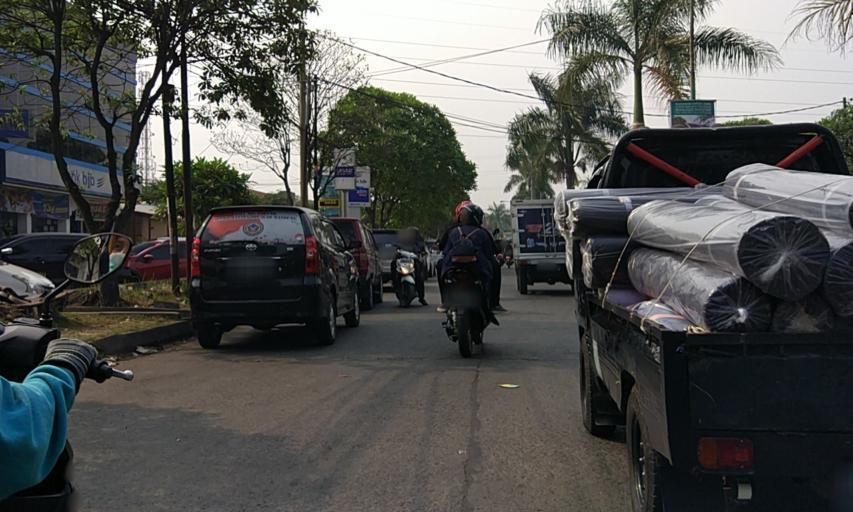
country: ID
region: West Java
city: Margahayukencana
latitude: -6.9549
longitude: 107.5621
